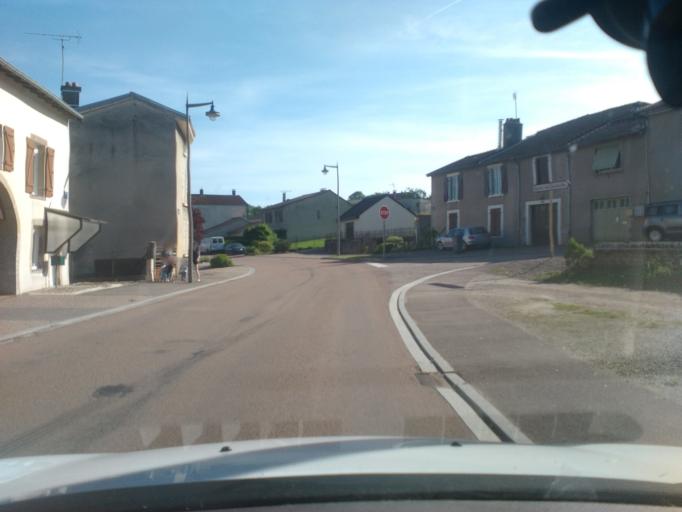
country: FR
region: Lorraine
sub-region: Departement des Vosges
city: Mirecourt
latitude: 48.2246
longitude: 6.2196
